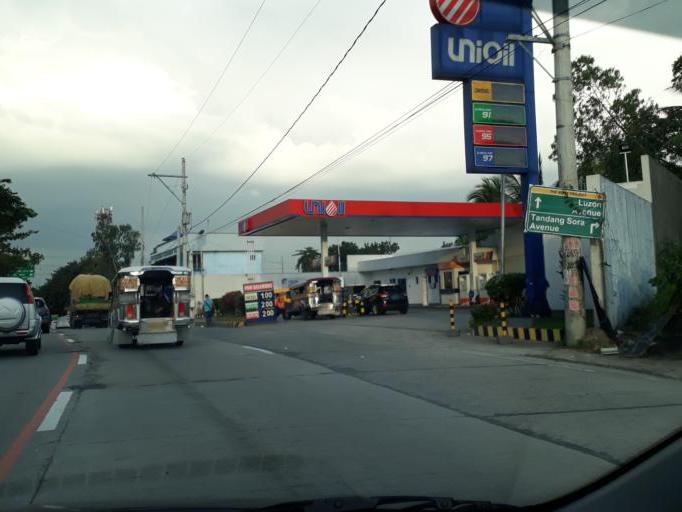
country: PH
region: Calabarzon
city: Bagong Pagasa
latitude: 14.6727
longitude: 121.0469
